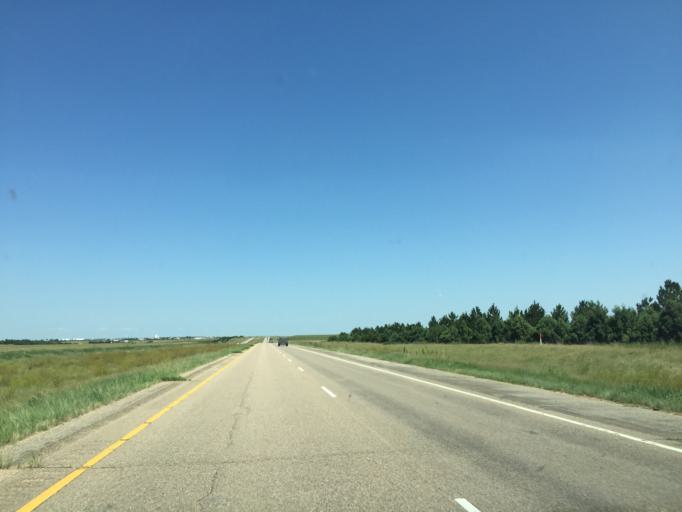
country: US
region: Colorado
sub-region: Kit Carson County
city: Burlington
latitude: 39.2941
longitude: -102.3665
